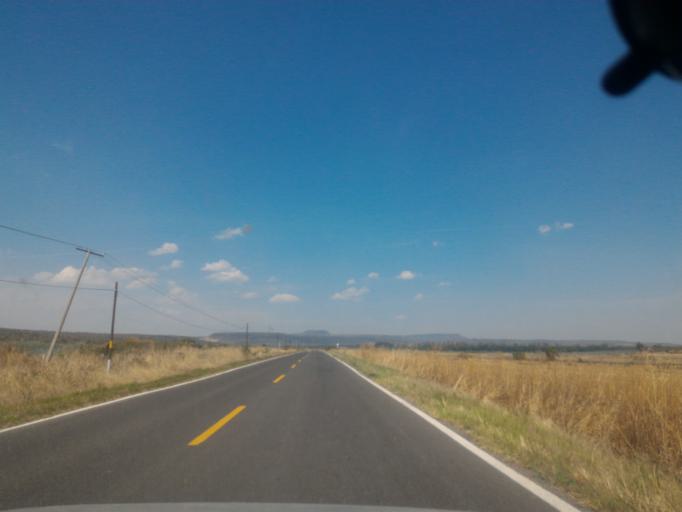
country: MX
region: Guanajuato
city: Ciudad Manuel Doblado
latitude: 20.8545
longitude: -101.9990
